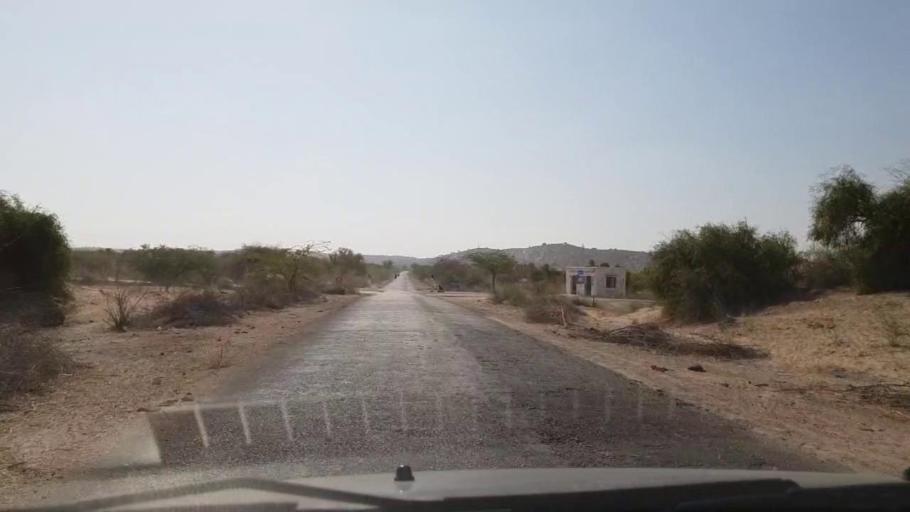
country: PK
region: Sindh
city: Mithi
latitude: 24.6523
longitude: 69.7520
